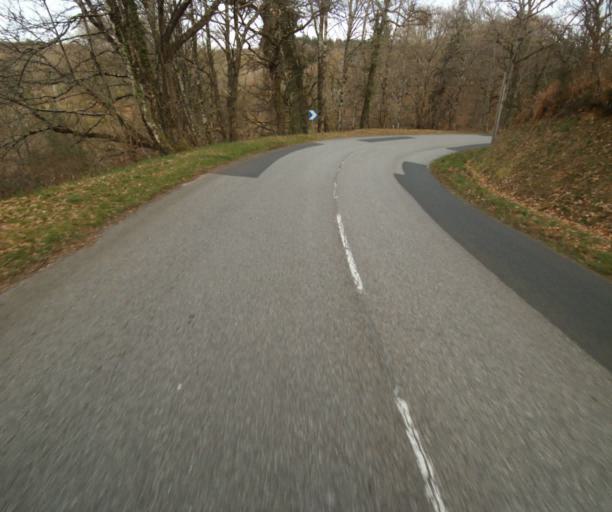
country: FR
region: Limousin
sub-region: Departement de la Correze
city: Treignac
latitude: 45.4455
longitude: 1.8053
